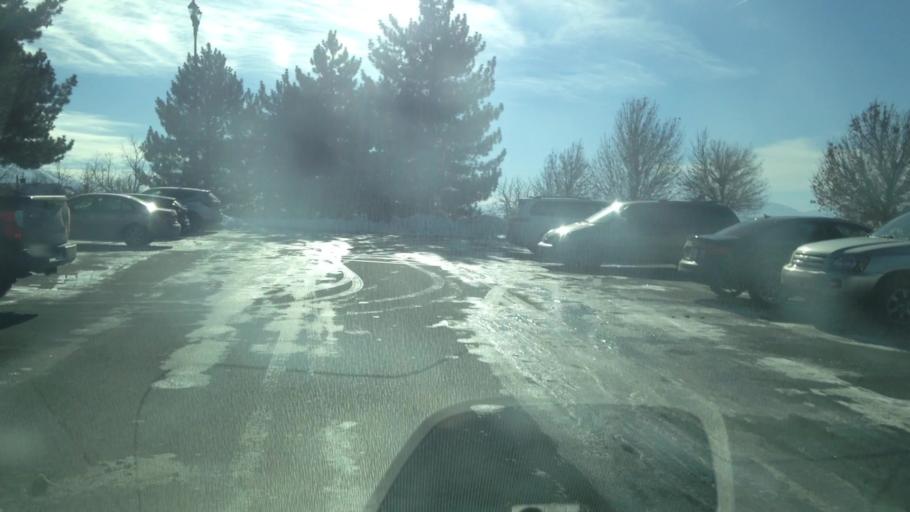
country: US
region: Utah
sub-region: Cache County
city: Logan
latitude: 41.7340
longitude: -111.8287
